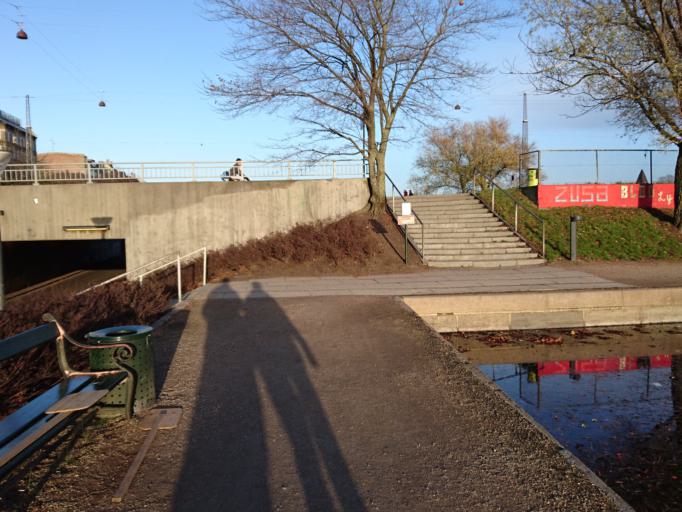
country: DK
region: Capital Region
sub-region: Kobenhavn
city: Copenhagen
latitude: 55.6917
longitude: 12.5691
